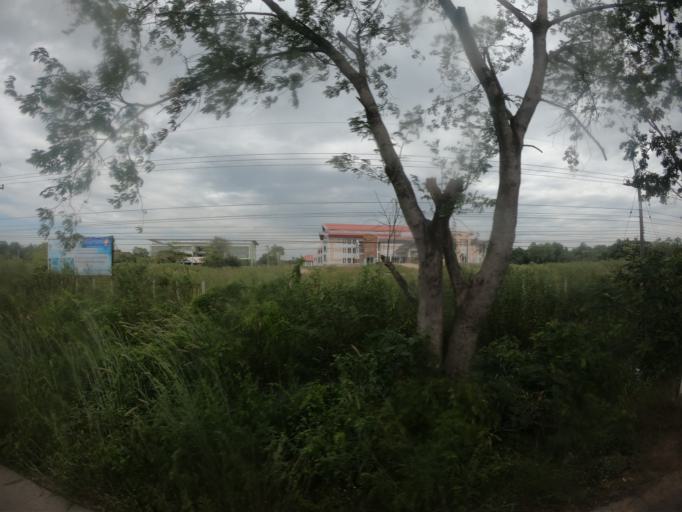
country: TH
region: Maha Sarakham
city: Kantharawichai
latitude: 16.3396
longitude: 103.2072
